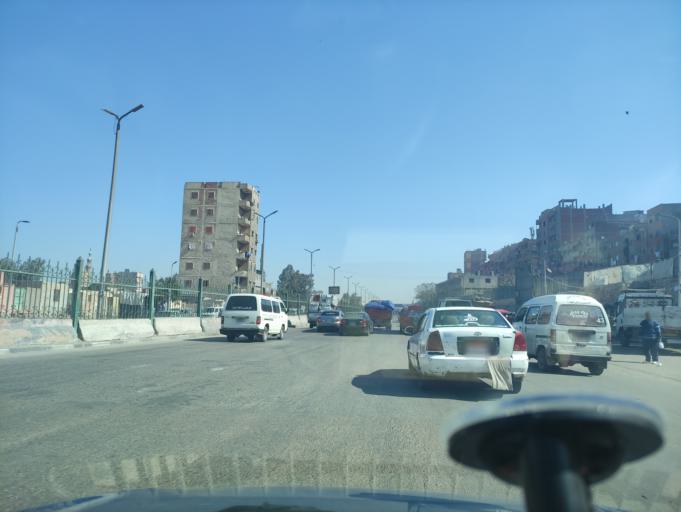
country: EG
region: Muhafazat al Qahirah
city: Cairo
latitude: 30.0405
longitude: 31.2744
